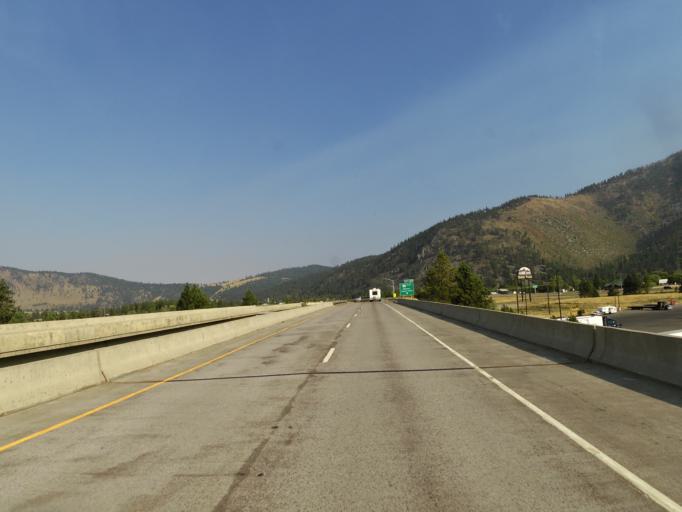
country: US
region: Montana
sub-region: Missoula County
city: Bonner-West Riverside
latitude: 46.8733
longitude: -113.8887
